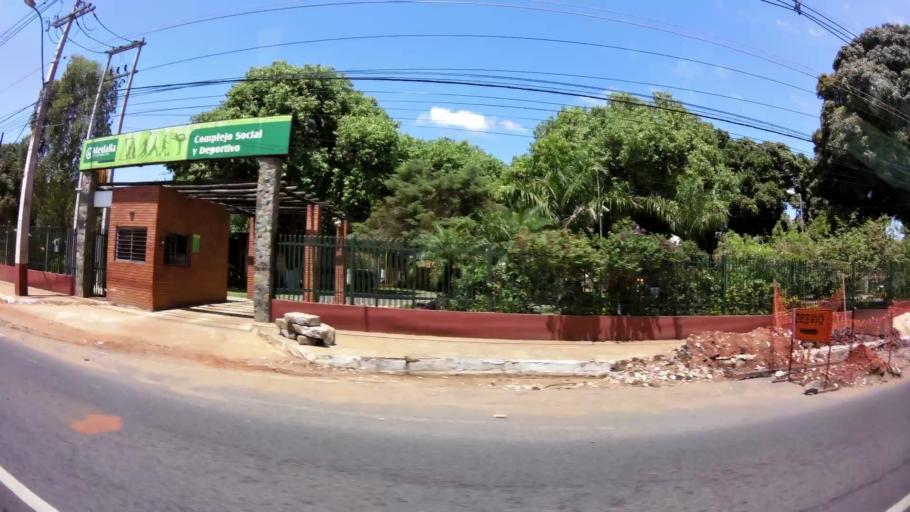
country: PY
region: Central
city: Lambare
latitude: -25.3269
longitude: -57.5689
